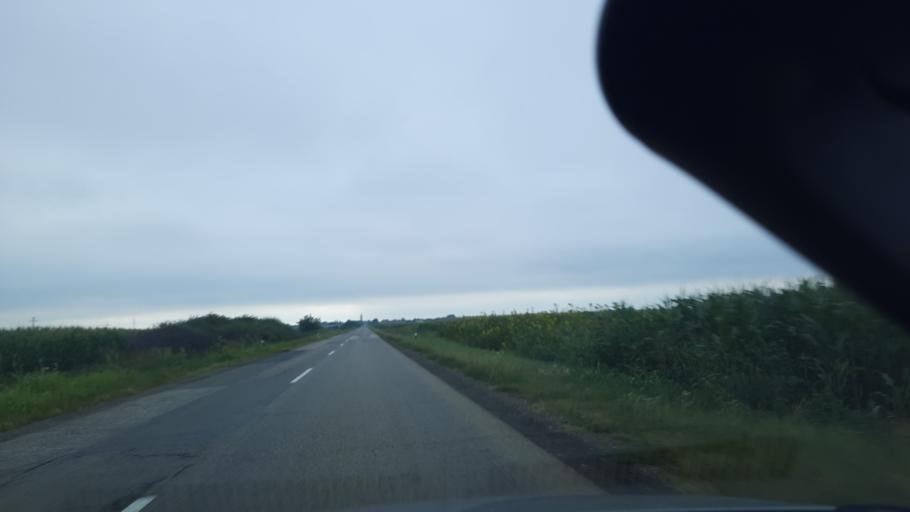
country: RS
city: Farkazdin
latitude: 45.1953
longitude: 20.4536
